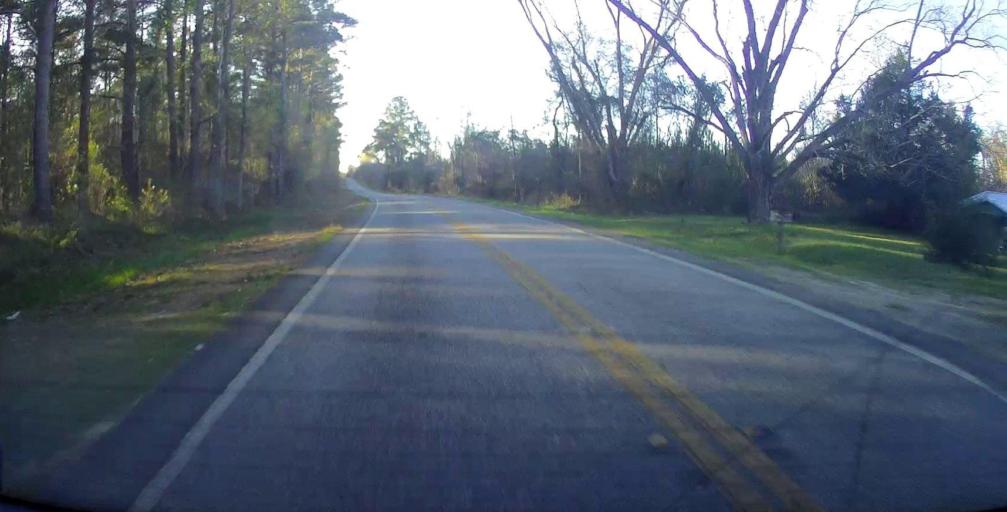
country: US
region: Georgia
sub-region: Wilcox County
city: Abbeville
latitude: 32.1027
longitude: -83.3060
